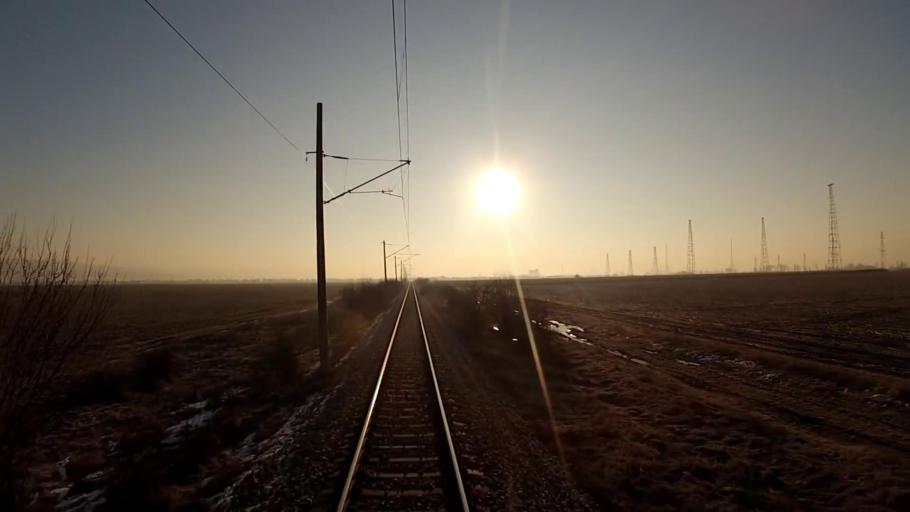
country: BG
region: Sofiya
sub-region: Obshtina Kostinbrod
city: Kostinbrod
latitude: 42.8111
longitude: 23.1930
